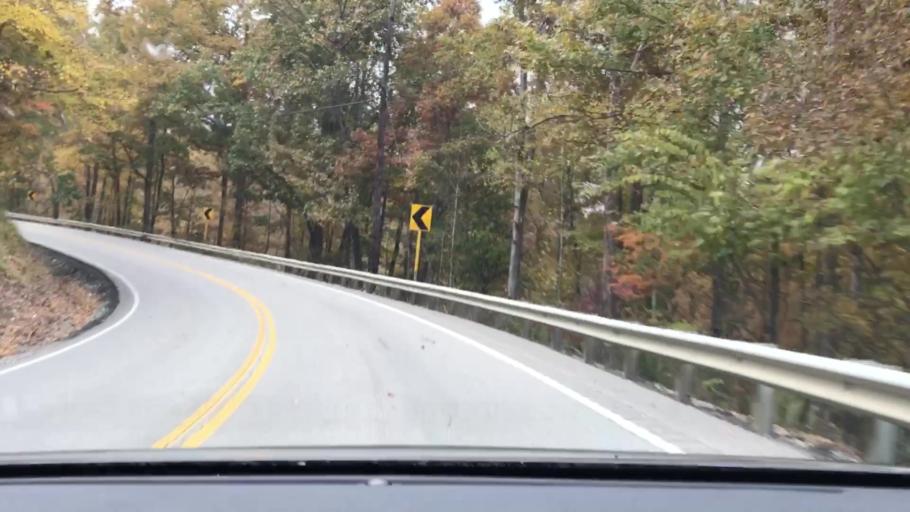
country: US
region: Tennessee
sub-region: Scott County
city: Huntsville
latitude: 36.3384
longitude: -84.6156
